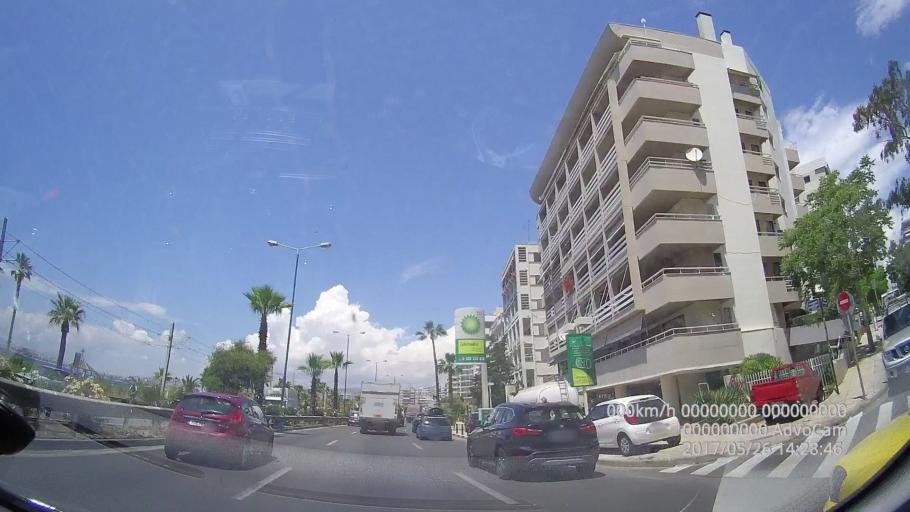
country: GR
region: Attica
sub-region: Nomarchia Athinas
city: Metamorfosi
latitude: 38.0722
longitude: 23.7687
